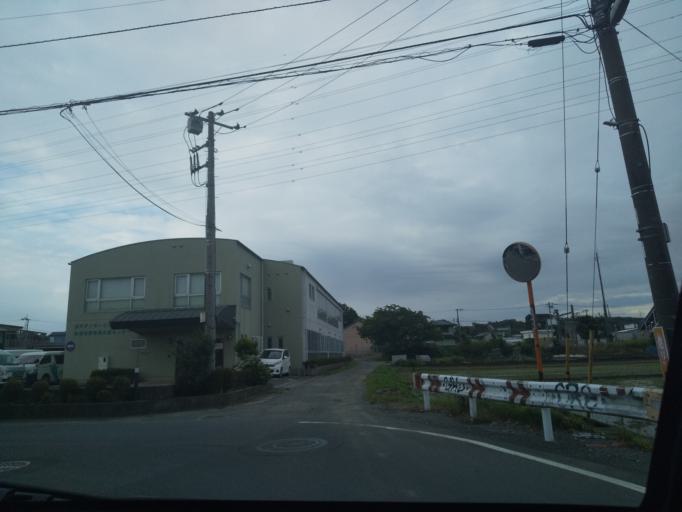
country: JP
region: Kanagawa
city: Zama
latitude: 35.4952
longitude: 139.3857
